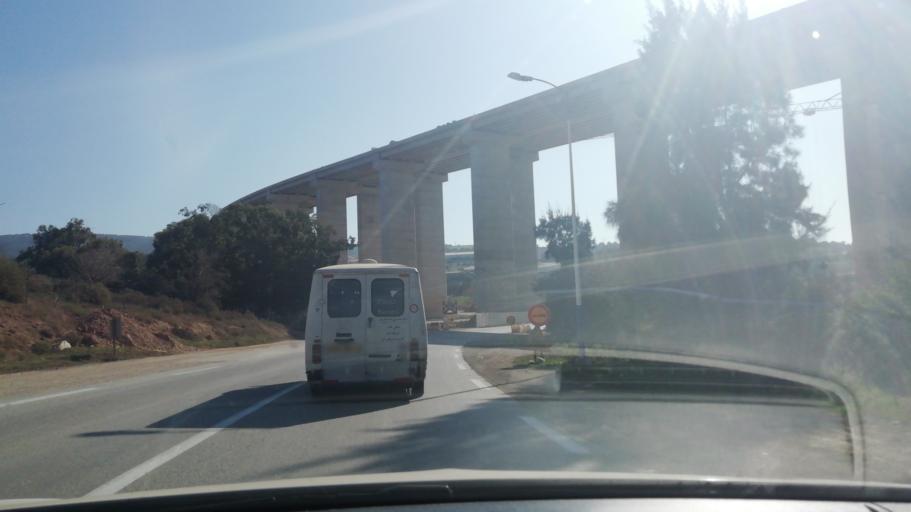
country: DZ
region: Tlemcen
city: Nedroma
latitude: 35.1056
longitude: -1.8342
